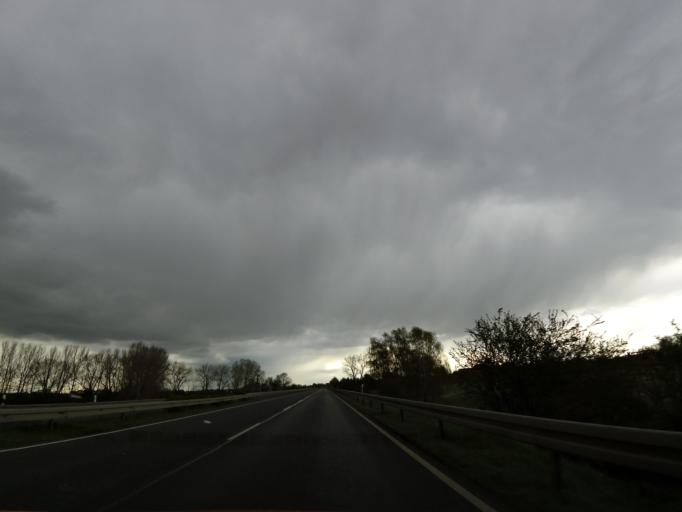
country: DE
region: Saxony-Anhalt
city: Egeln
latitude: 51.9471
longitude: 11.4226
